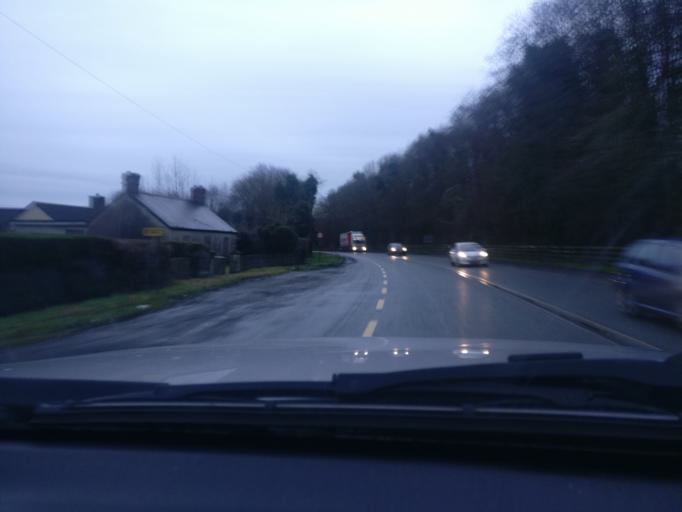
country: IE
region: Leinster
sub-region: An Mhi
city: Navan
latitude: 53.6587
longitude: -6.7208
